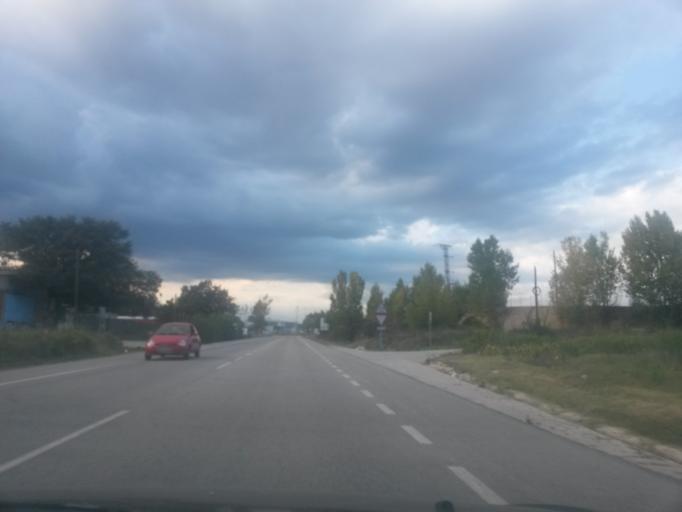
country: ES
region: Catalonia
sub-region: Provincia de Girona
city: Vilobi d'Onyar
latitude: 41.8970
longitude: 2.7725
